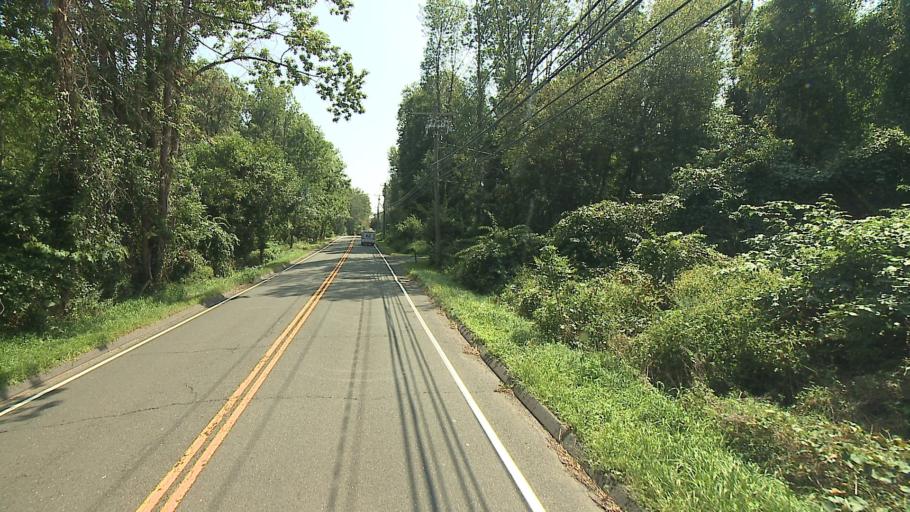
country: US
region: Connecticut
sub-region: Fairfield County
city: Georgetown
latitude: 41.2329
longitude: -73.4044
